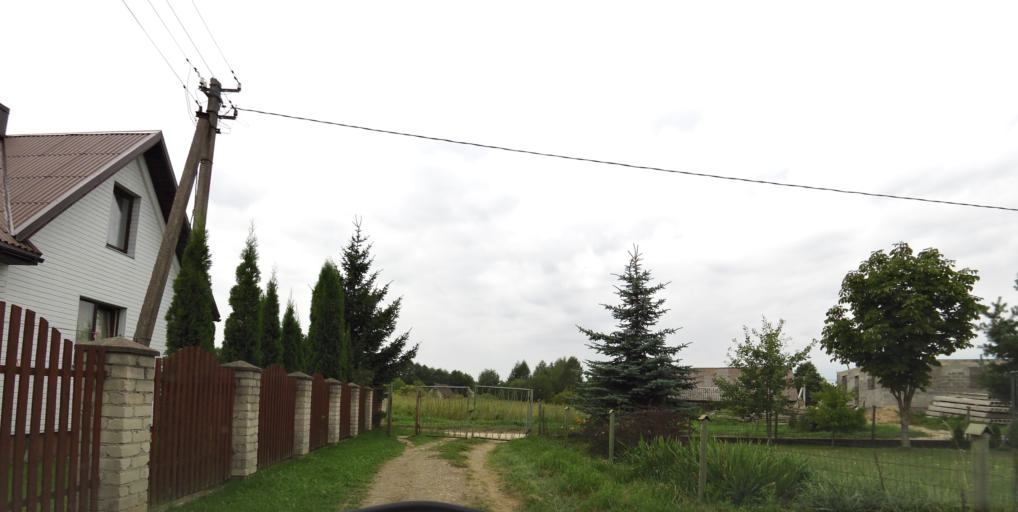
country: LT
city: Grigiskes
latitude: 54.7667
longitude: 25.0237
